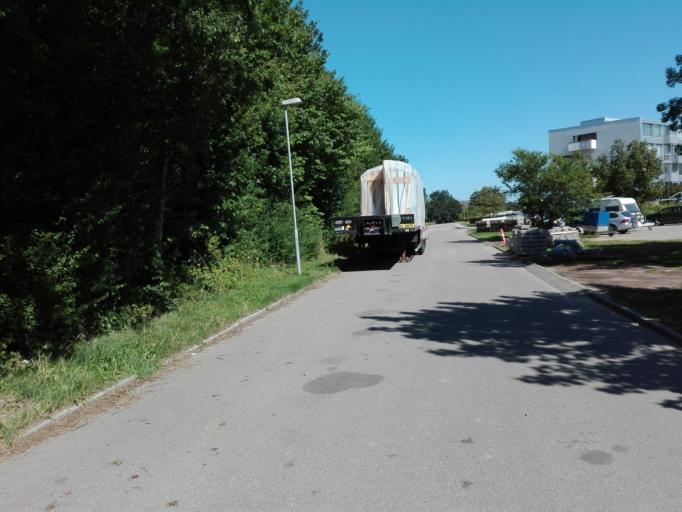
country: DK
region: Central Jutland
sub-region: Arhus Kommune
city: Stavtrup
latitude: 56.1163
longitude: 10.1443
